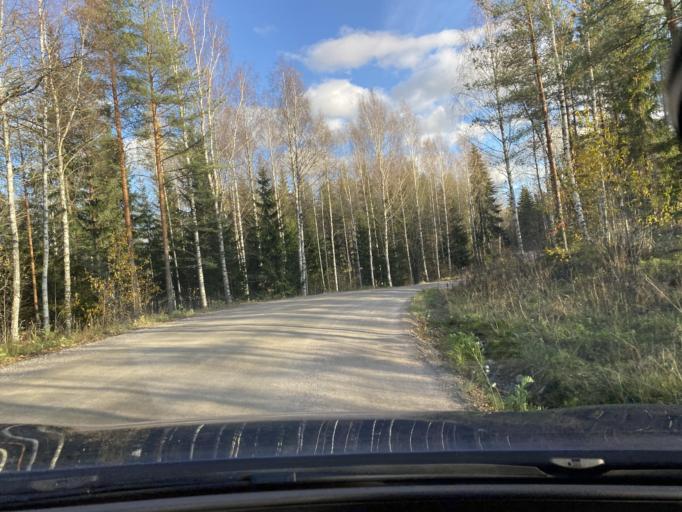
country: FI
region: Uusimaa
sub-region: Porvoo
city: Pukkila
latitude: 60.7532
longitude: 25.5406
